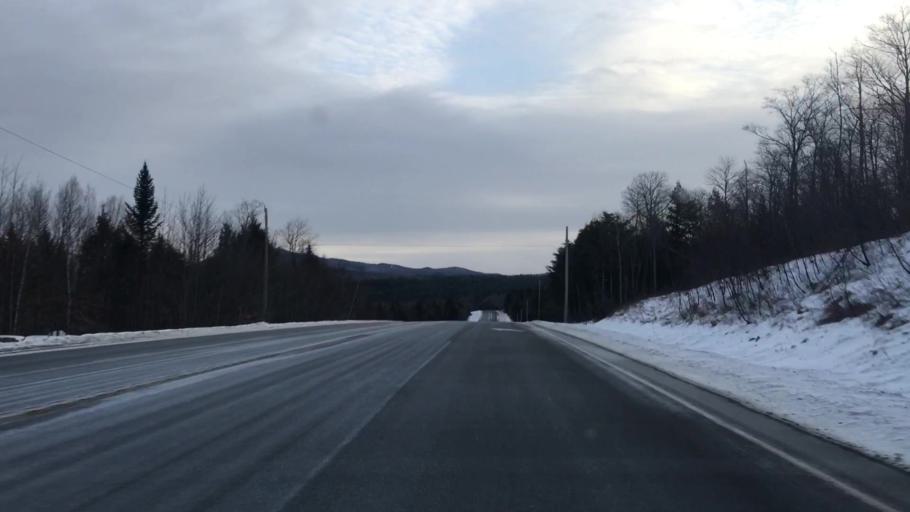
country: US
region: Maine
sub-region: Hancock County
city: Franklin
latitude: 44.8317
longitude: -68.2151
